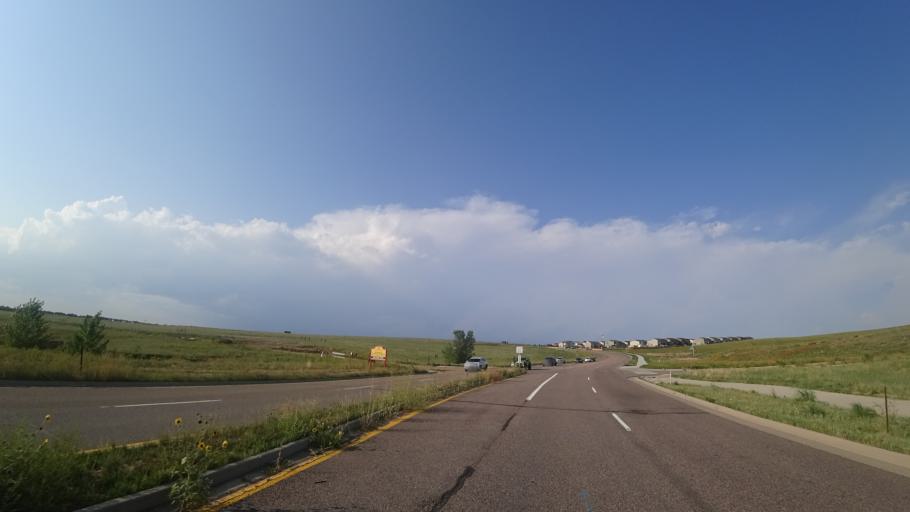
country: US
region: Colorado
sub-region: Arapahoe County
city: Dove Valley
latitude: 39.6332
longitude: -104.7378
